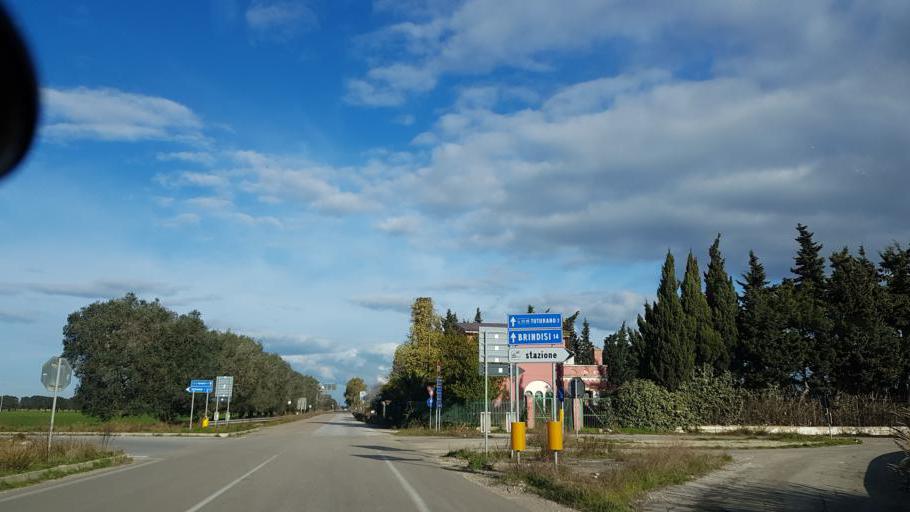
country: IT
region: Apulia
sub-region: Provincia di Brindisi
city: Tuturano
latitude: 40.5499
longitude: 17.9760
